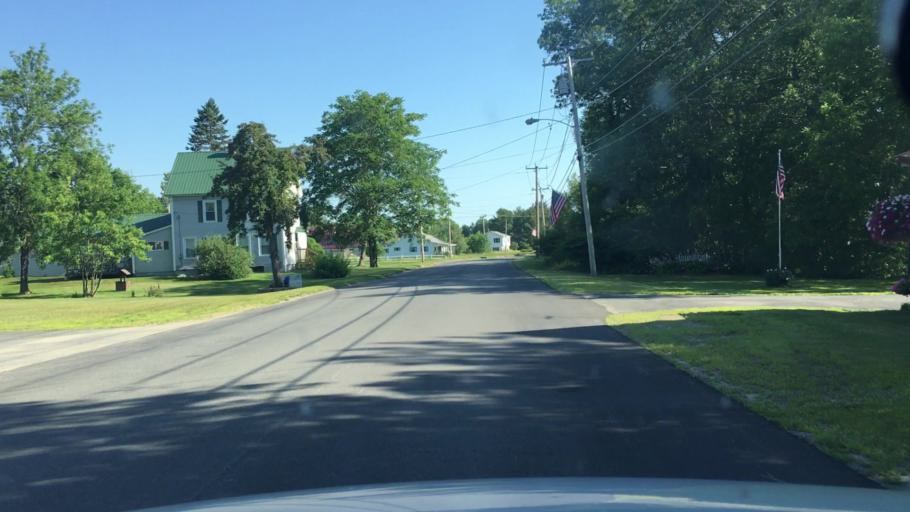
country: US
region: Maine
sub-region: Penobscot County
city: Howland
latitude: 45.2353
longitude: -68.6491
